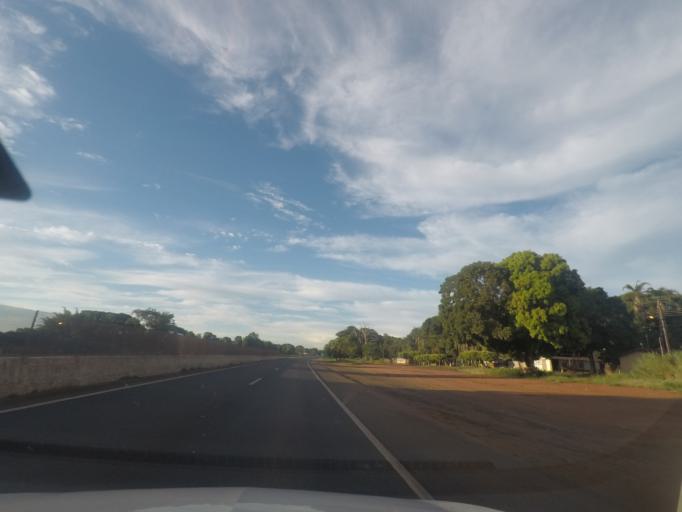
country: BR
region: Goias
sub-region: Goiatuba
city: Goiatuba
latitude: -18.0596
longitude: -49.2694
